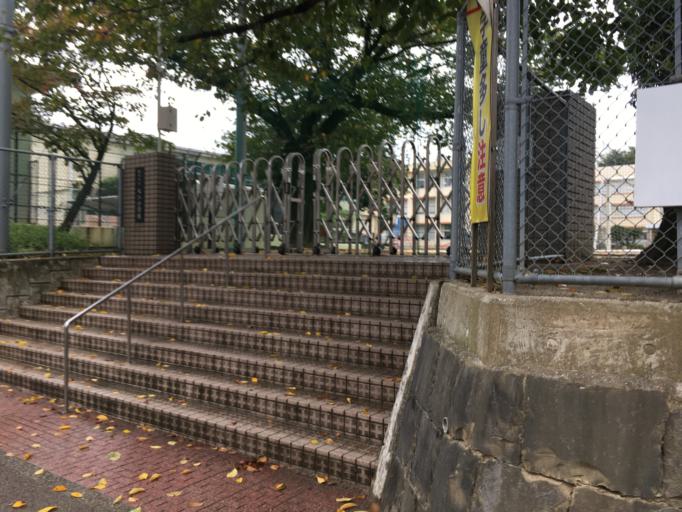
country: JP
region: Kumamoto
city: Kumamoto
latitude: 32.8011
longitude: 130.7260
